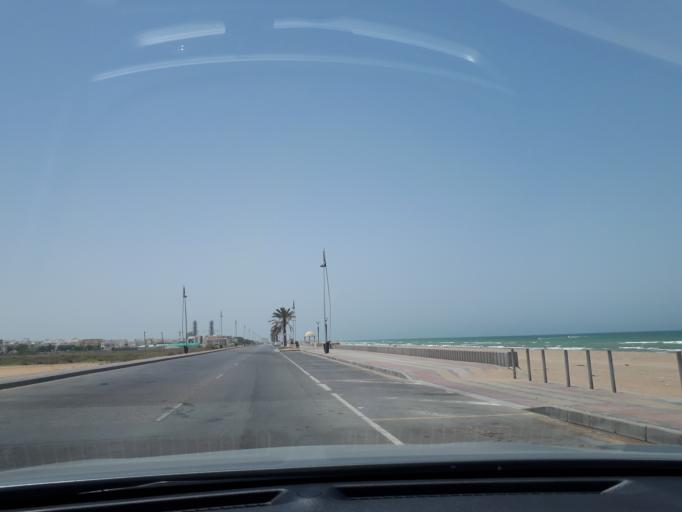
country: OM
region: Muhafazat Masqat
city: As Sib al Jadidah
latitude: 23.6400
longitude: 58.2480
